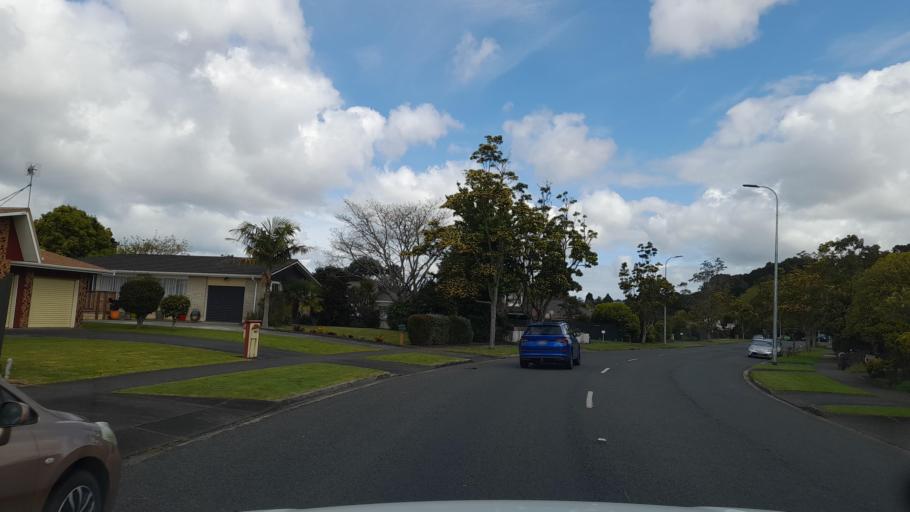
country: NZ
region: Northland
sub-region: Whangarei
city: Whangarei
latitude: -35.6884
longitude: 174.3007
